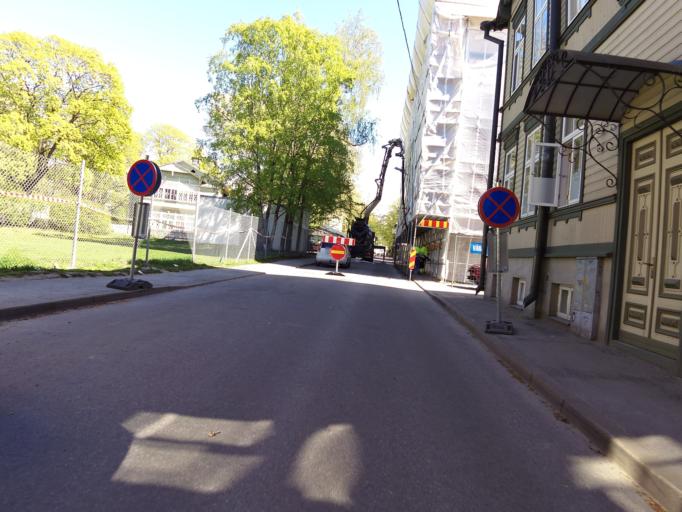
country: EE
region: Harju
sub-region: Tallinna linn
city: Tallinn
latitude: 59.4380
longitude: 24.7772
